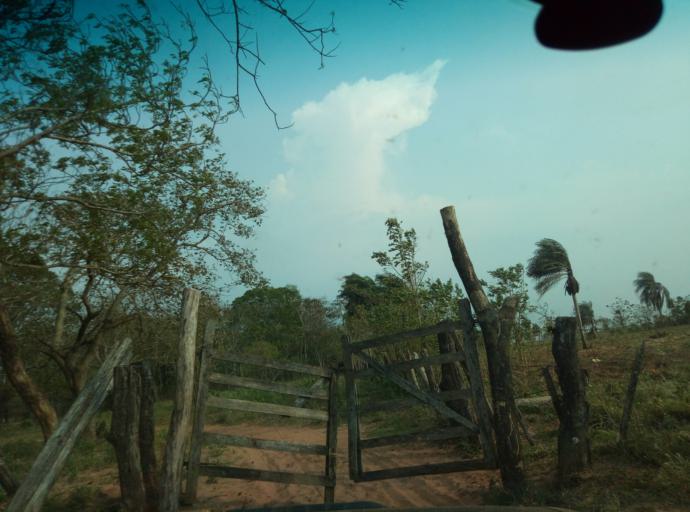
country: PY
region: Caaguazu
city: San Joaquin
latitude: -25.1489
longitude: -56.1021
